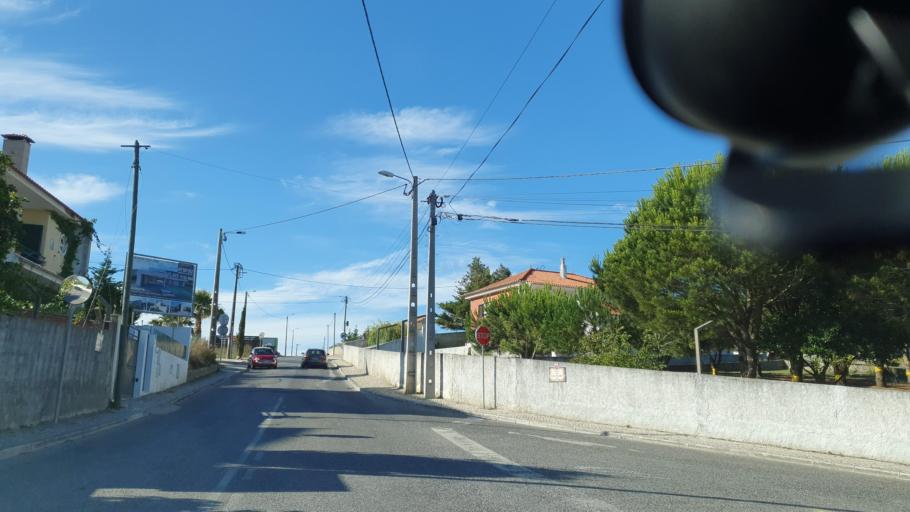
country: PT
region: Lisbon
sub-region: Sintra
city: Belas
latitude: 38.7990
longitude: -9.2533
